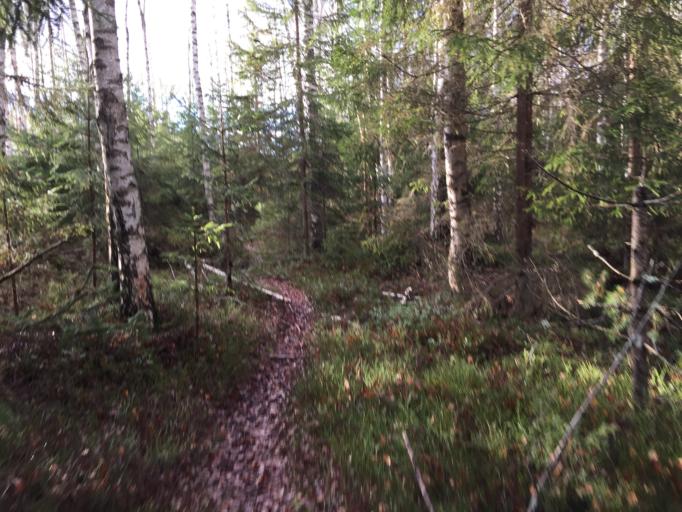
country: LV
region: Koceni
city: Koceni
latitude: 57.5379
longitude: 25.3758
